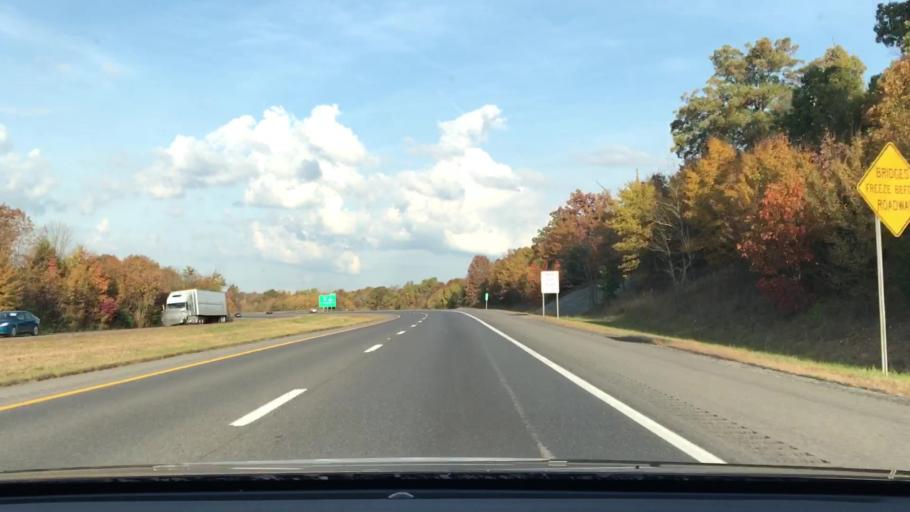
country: US
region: Kentucky
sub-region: Lyon County
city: Eddyville
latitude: 37.0629
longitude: -88.0425
